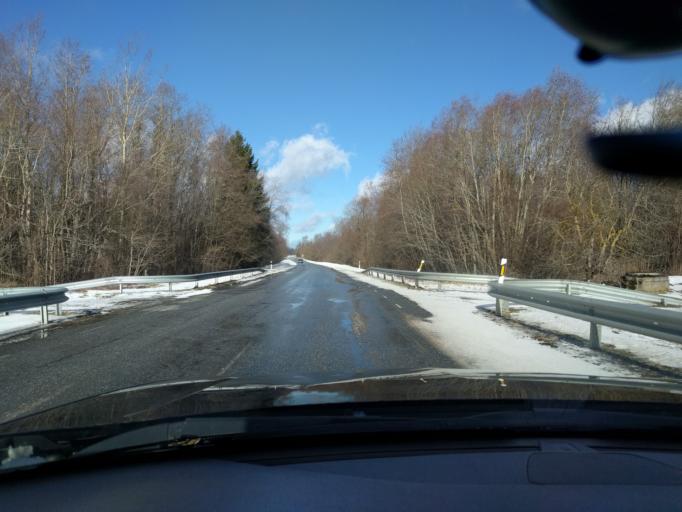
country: EE
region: Harju
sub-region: Raasiku vald
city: Raasiku
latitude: 59.3049
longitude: 25.1702
